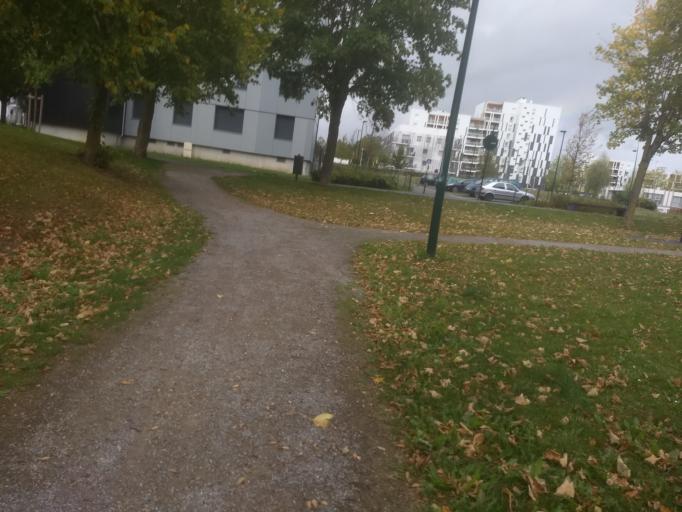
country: FR
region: Nord-Pas-de-Calais
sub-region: Departement du Pas-de-Calais
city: Saint-Nicolas
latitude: 50.3036
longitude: 2.7941
